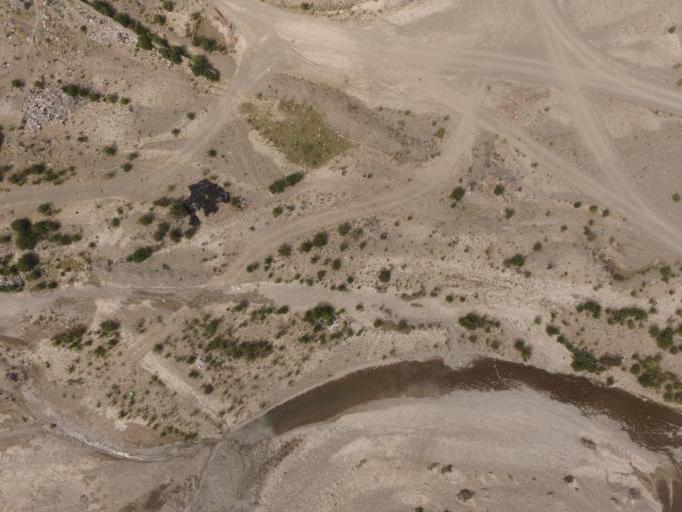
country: BO
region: Oruro
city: Challapata
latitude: -18.6923
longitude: -66.7588
